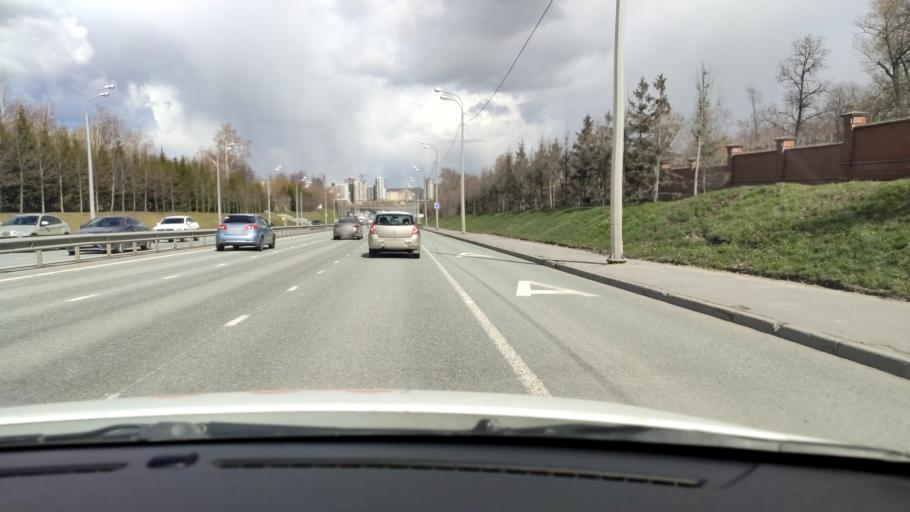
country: RU
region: Tatarstan
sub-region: Gorod Kazan'
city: Kazan
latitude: 55.8009
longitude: 49.1529
